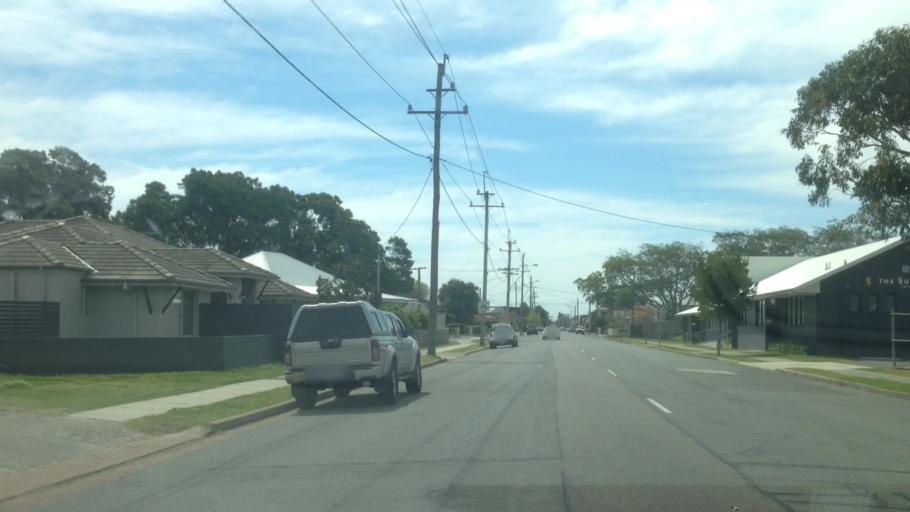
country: AU
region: New South Wales
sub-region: Newcastle
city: Broadmeadow
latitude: -32.9282
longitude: 151.7366
